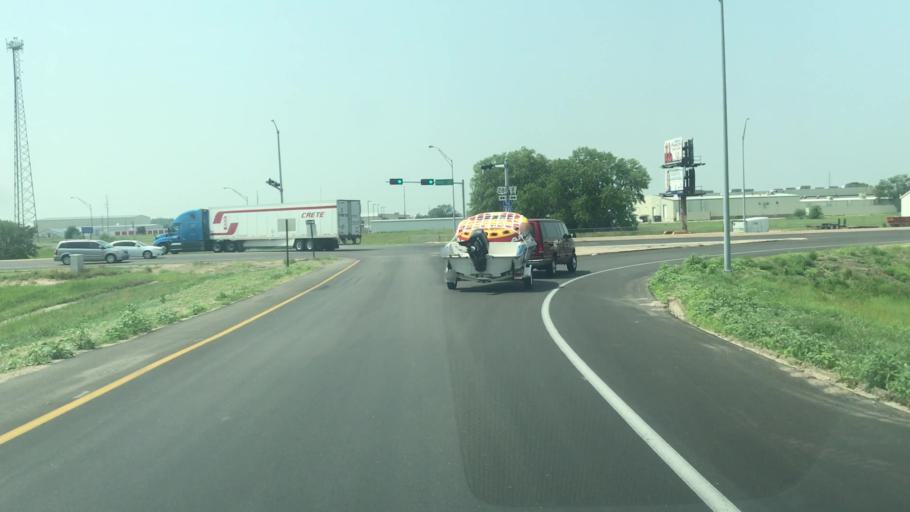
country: US
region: Nebraska
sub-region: Hall County
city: Grand Island
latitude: 40.9150
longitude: -98.3825
